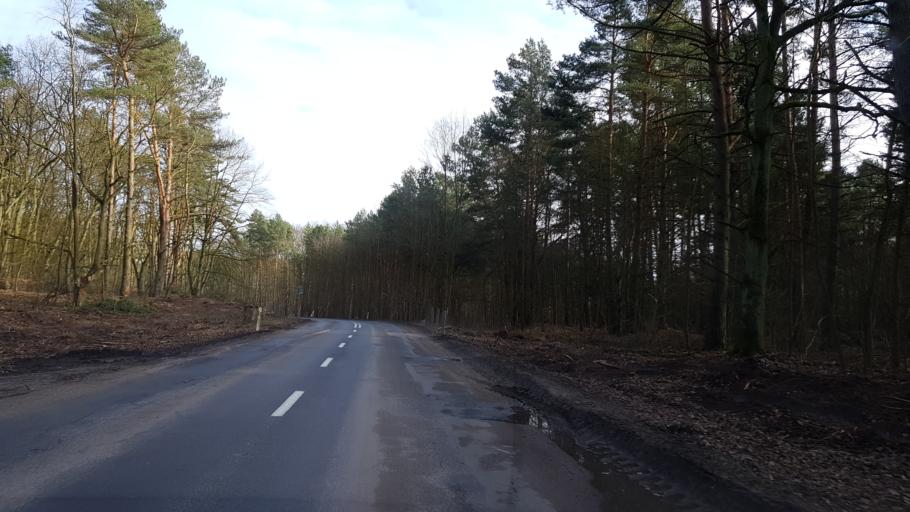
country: PL
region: West Pomeranian Voivodeship
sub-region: Szczecin
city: Szczecin
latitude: 53.4725
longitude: 14.4752
